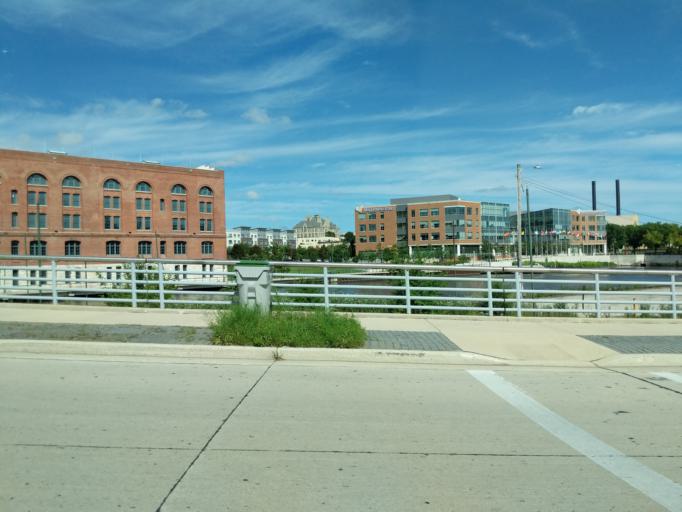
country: US
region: Wisconsin
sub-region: Milwaukee County
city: Milwaukee
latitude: 43.0468
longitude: -87.9124
